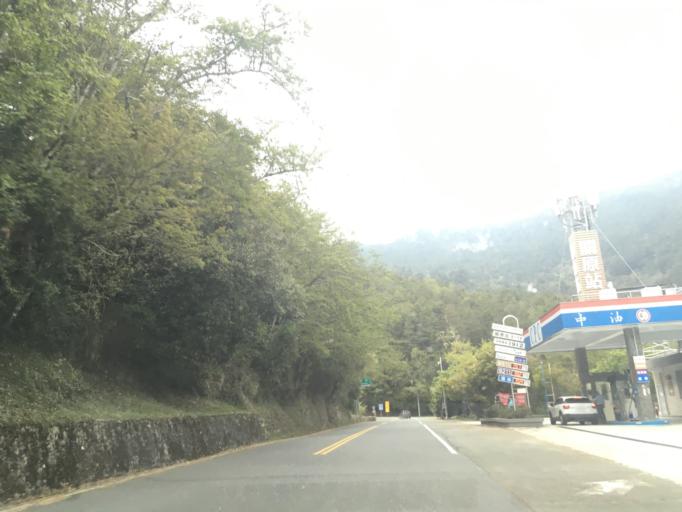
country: TW
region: Taiwan
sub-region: Hualien
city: Hualian
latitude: 24.1846
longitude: 121.3422
